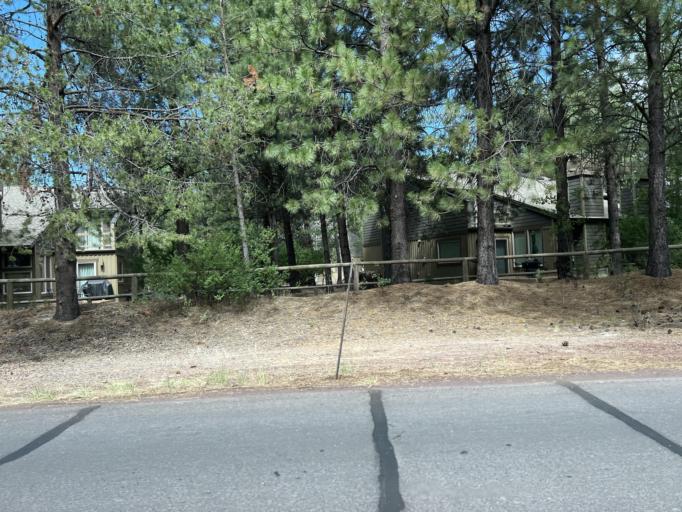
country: US
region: Oregon
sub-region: Deschutes County
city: Sunriver
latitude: 43.8826
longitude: -121.4409
